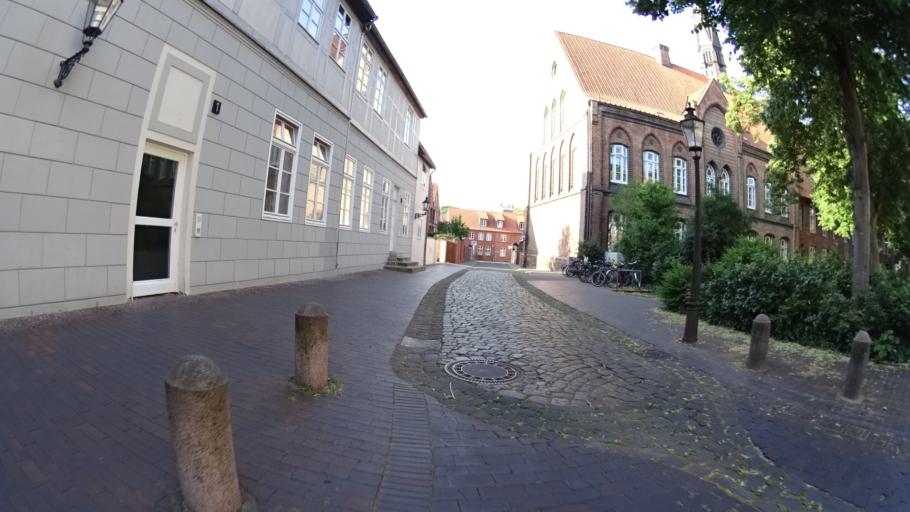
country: DE
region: Lower Saxony
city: Lueneburg
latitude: 53.2466
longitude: 10.4052
